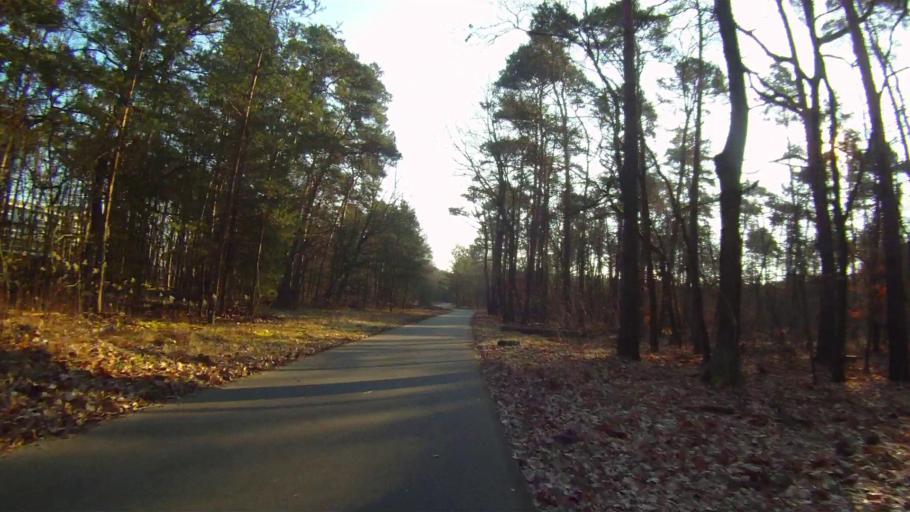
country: DE
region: Berlin
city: Friedrichshagen
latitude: 52.4253
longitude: 13.6375
